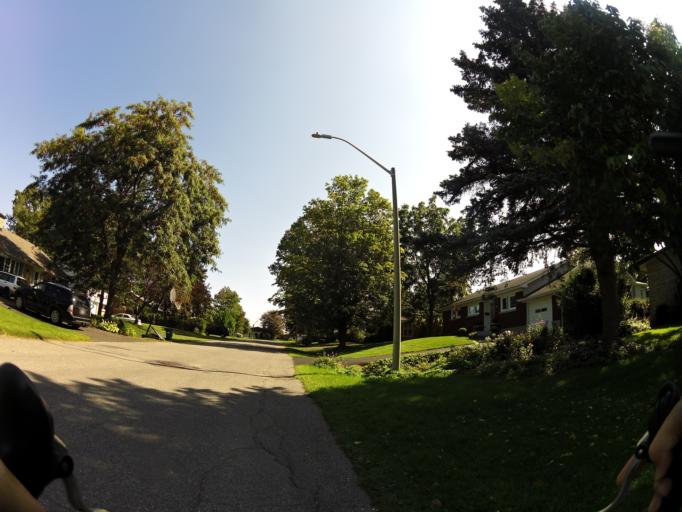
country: CA
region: Ontario
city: Ottawa
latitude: 45.3958
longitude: -75.6529
